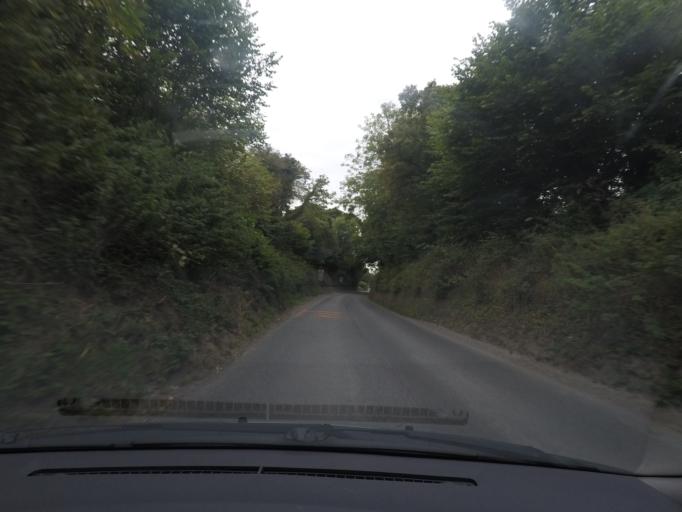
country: GB
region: England
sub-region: Wiltshire
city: Huish
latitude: 51.3693
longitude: -1.7727
